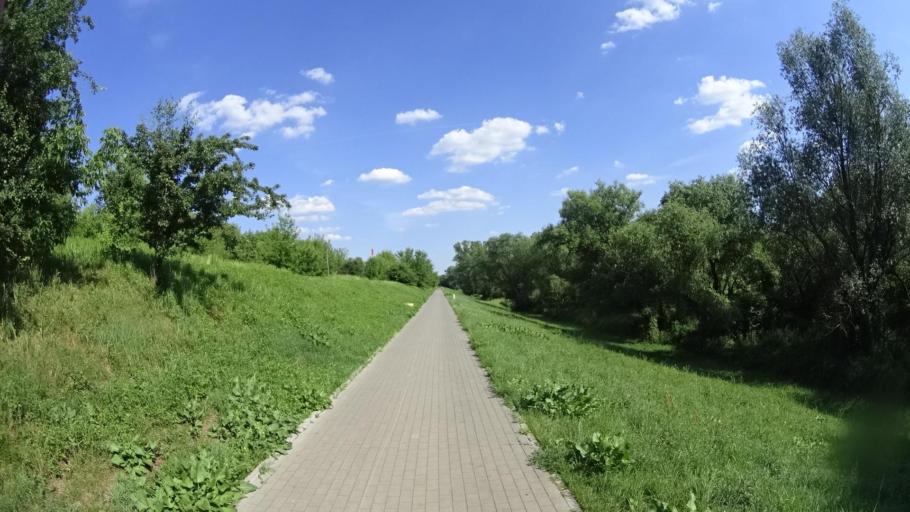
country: PL
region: Masovian Voivodeship
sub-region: Warszawa
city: Bialoleka
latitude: 52.3024
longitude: 20.9665
